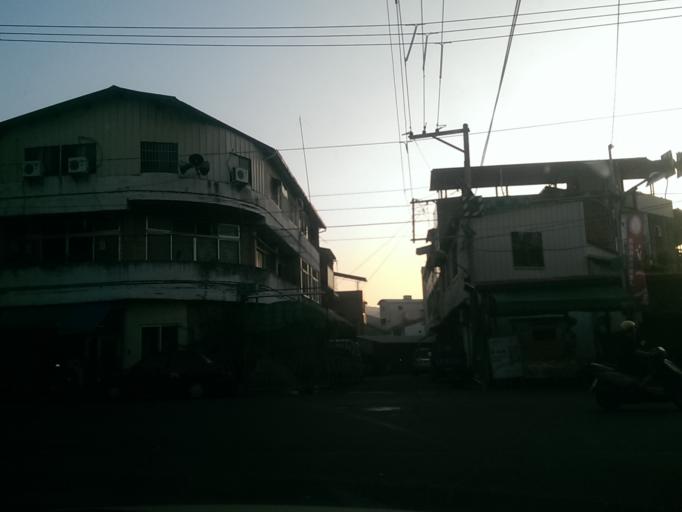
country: TW
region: Taiwan
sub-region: Nantou
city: Puli
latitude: 23.9624
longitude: 120.9661
